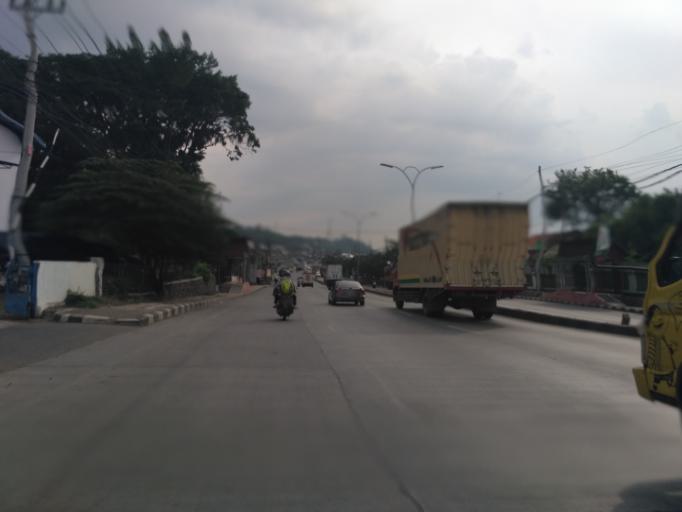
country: ID
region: Central Java
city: Semarang
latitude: -6.9858
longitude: 110.3466
